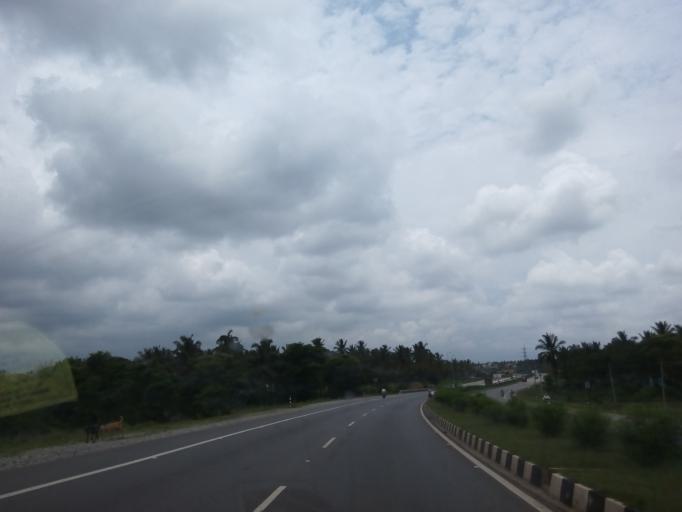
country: IN
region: Karnataka
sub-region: Hassan
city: Hassan
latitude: 12.9964
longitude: 76.1503
